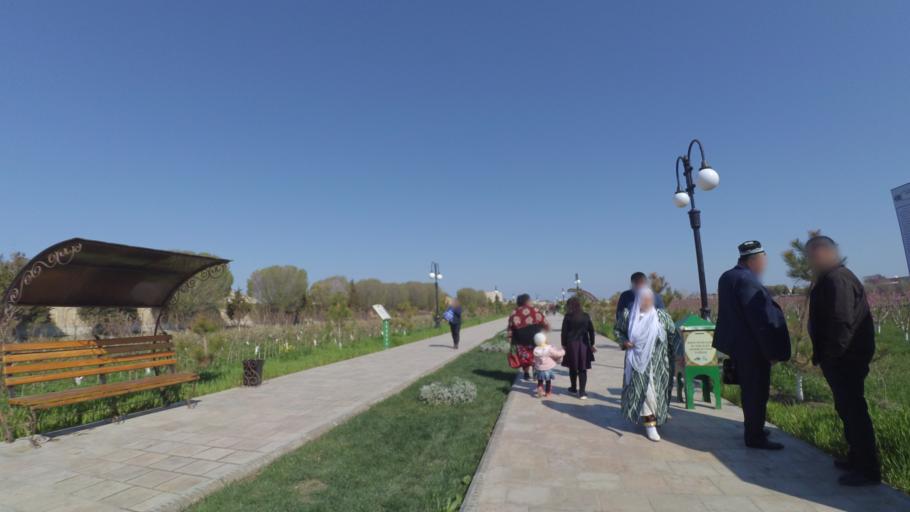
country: UZ
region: Bukhara
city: Kogon
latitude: 39.8007
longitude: 64.5388
